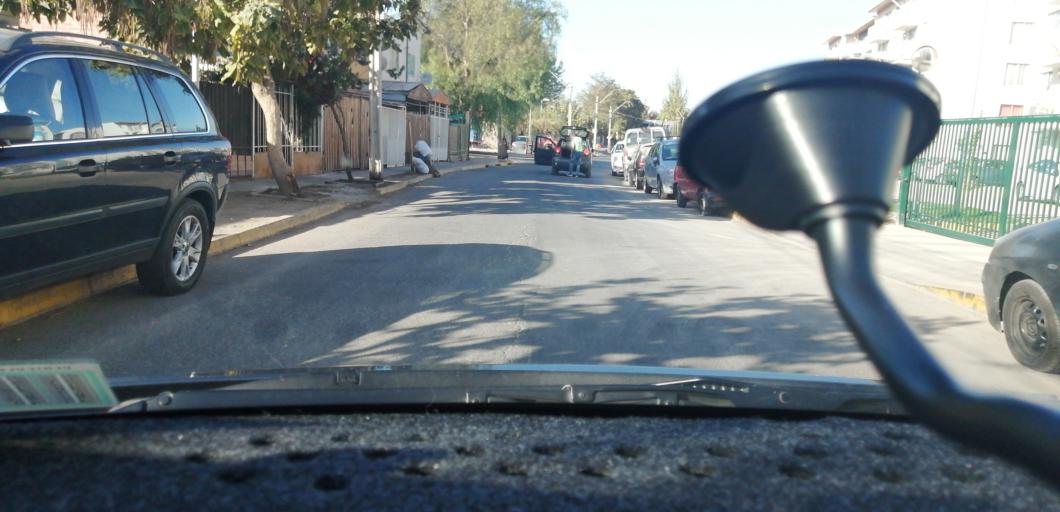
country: CL
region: Santiago Metropolitan
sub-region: Provincia de Santiago
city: Lo Prado
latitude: -33.4264
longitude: -70.7669
